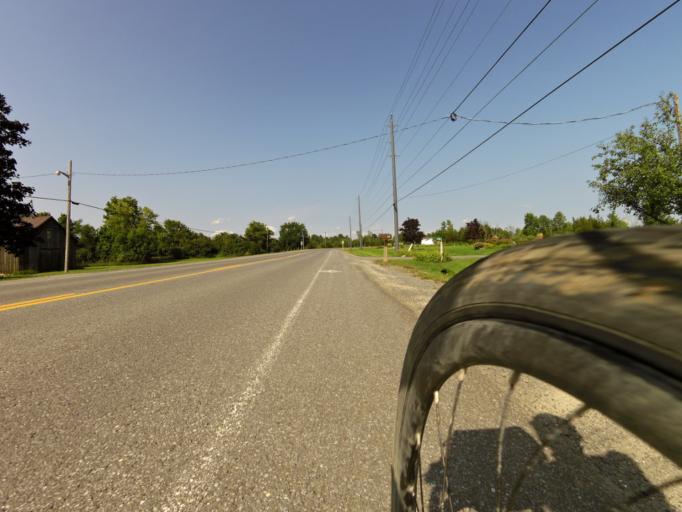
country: CA
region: Ontario
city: Kingston
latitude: 44.2991
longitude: -76.6992
